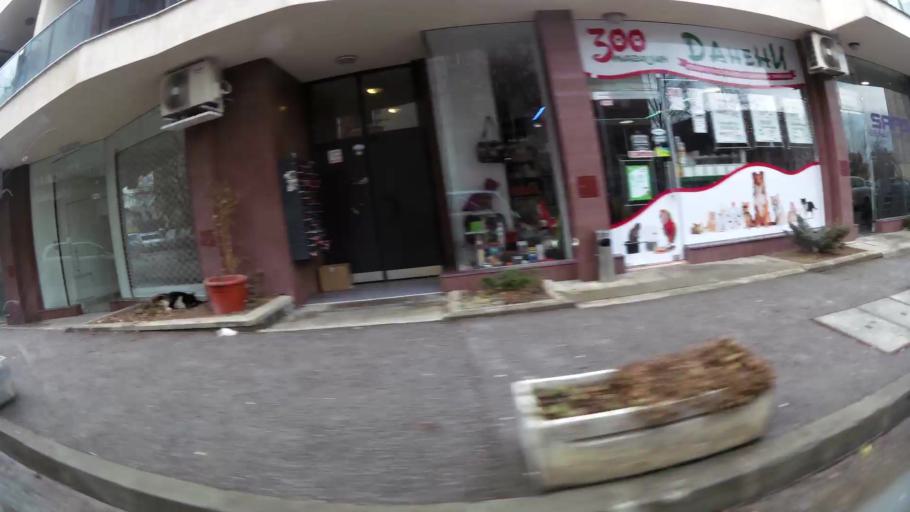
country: BG
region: Sofiya
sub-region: Obshtina Bozhurishte
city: Bozhurishte
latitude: 42.7232
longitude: 23.2522
